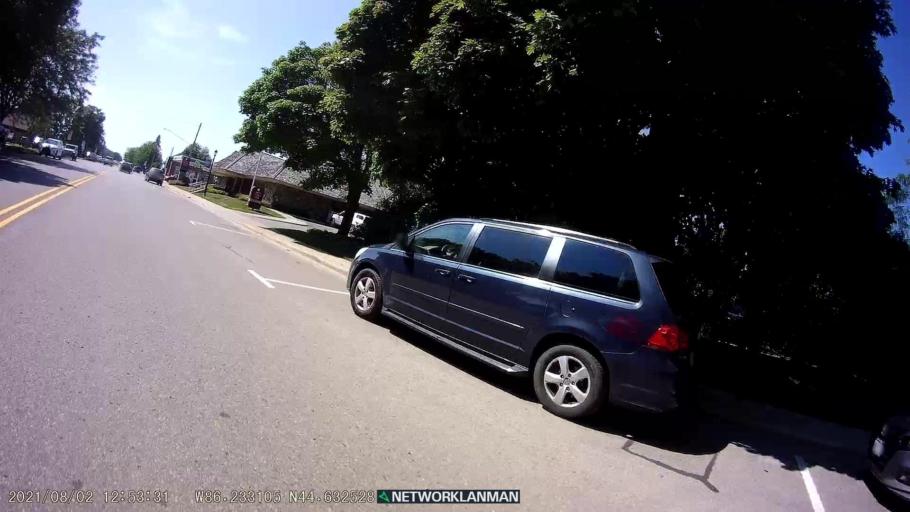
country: US
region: Michigan
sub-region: Benzie County
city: Frankfort
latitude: 44.6325
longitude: -86.2333
